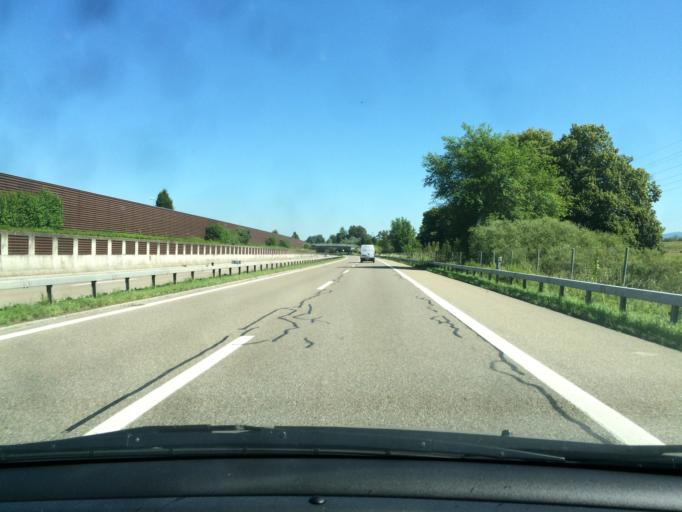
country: CH
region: Saint Gallen
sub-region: Wahlkreis Rheintal
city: Diepoldsau
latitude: 47.4003
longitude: 9.6474
